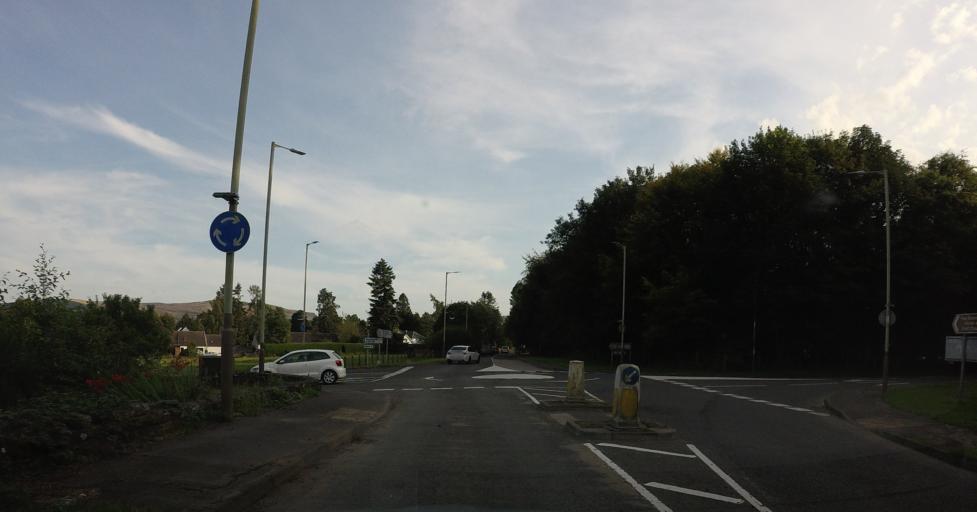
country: GB
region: Scotland
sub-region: Perth and Kinross
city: Auchterarder
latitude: 56.2860
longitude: -3.7455
